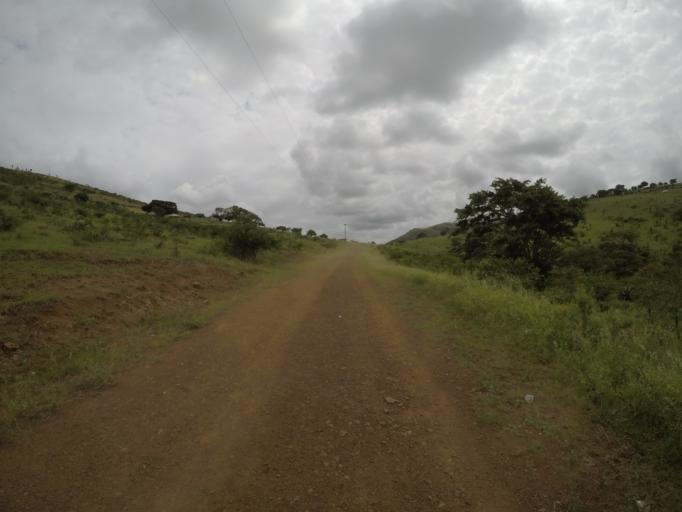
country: ZA
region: KwaZulu-Natal
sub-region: uThungulu District Municipality
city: Empangeni
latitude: -28.6205
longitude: 31.8914
